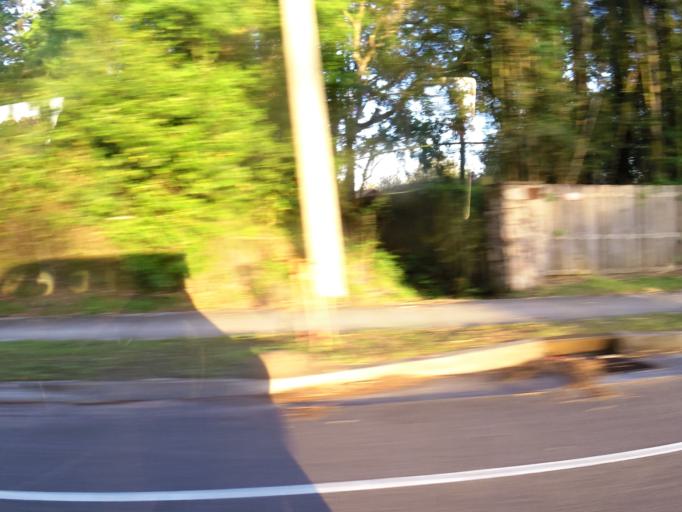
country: US
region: Florida
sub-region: Duval County
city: Jacksonville
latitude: 30.2680
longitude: -81.5714
